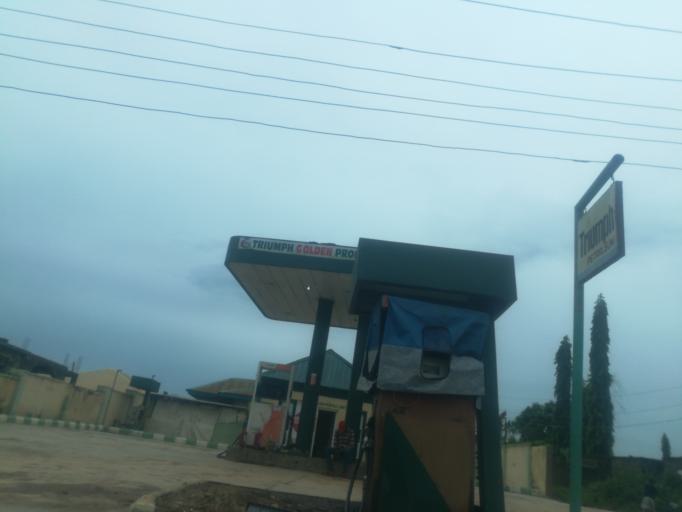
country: NG
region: Oyo
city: Ibadan
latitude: 7.3210
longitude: 3.8893
